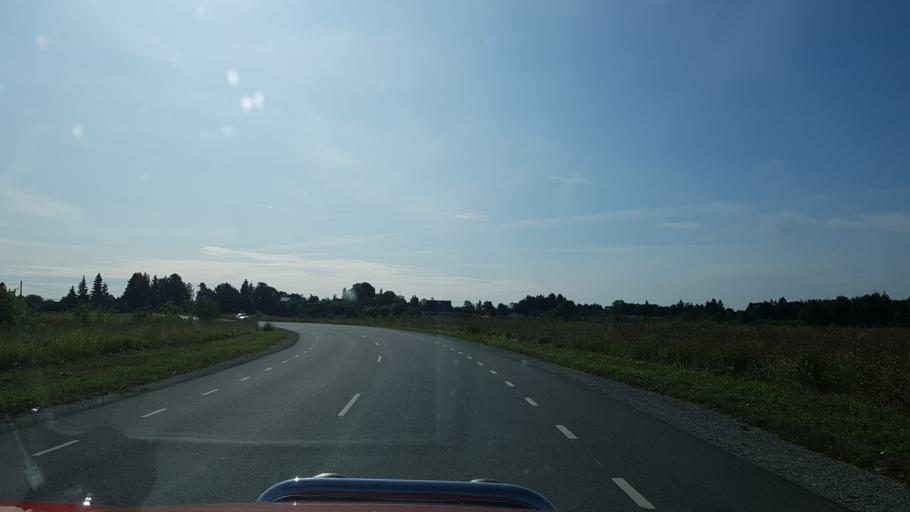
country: EE
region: Harju
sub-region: Joelaehtme vald
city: Loo
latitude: 59.3984
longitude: 24.9279
